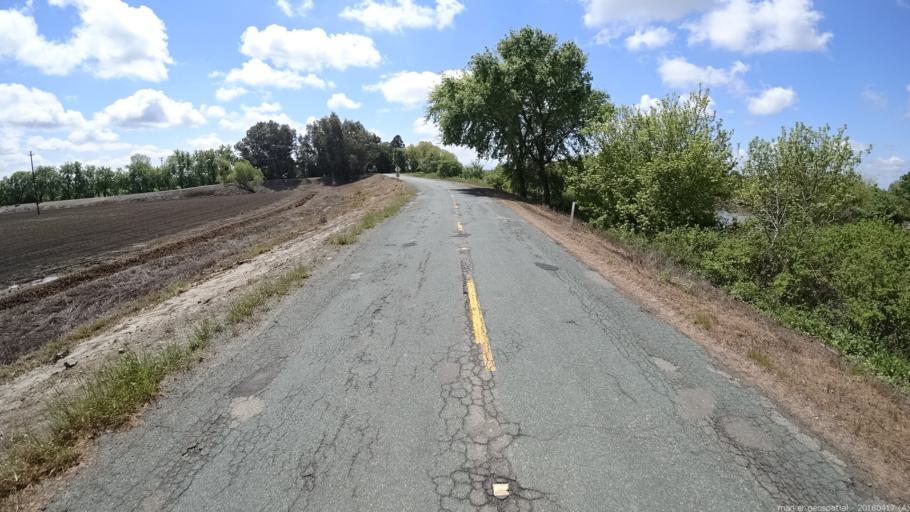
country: US
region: California
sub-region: Sacramento County
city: Walnut Grove
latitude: 38.1805
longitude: -121.5775
